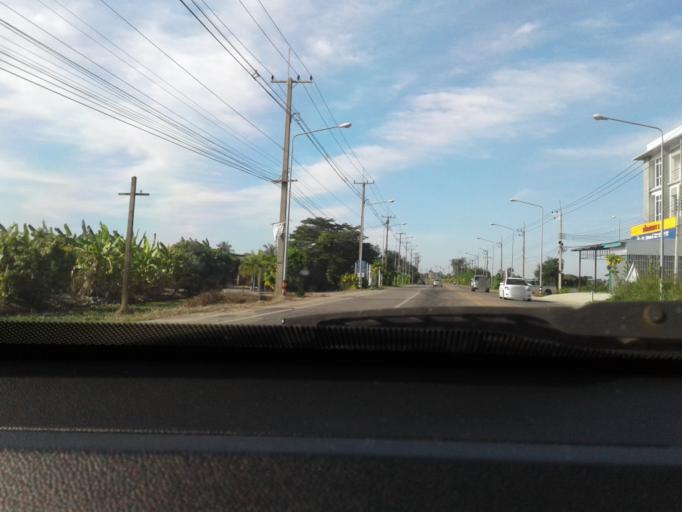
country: TH
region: Nonthaburi
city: Sai Noi
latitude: 13.9069
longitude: 100.2766
